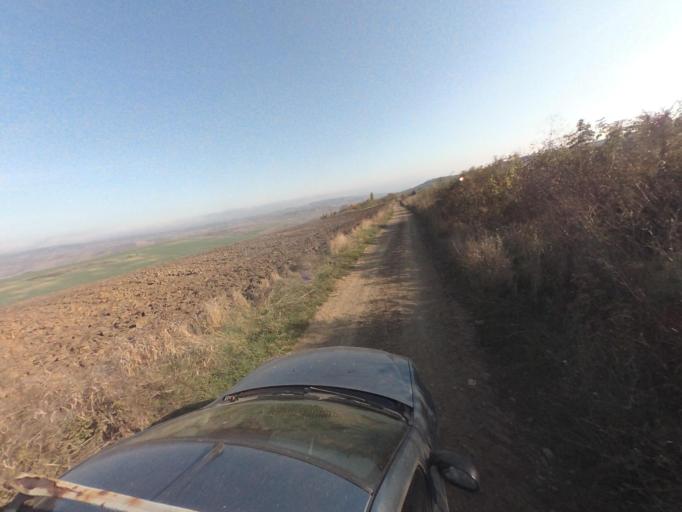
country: RO
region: Neamt
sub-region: Comuna Pancesti
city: Pancesti
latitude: 46.8779
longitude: 27.1918
